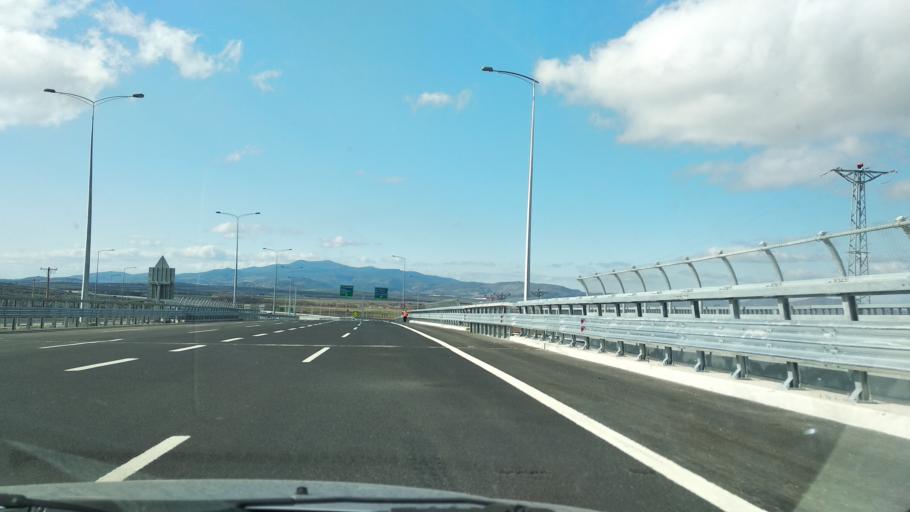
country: TR
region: Izmir
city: Zeytindag
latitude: 38.9736
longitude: 27.0512
